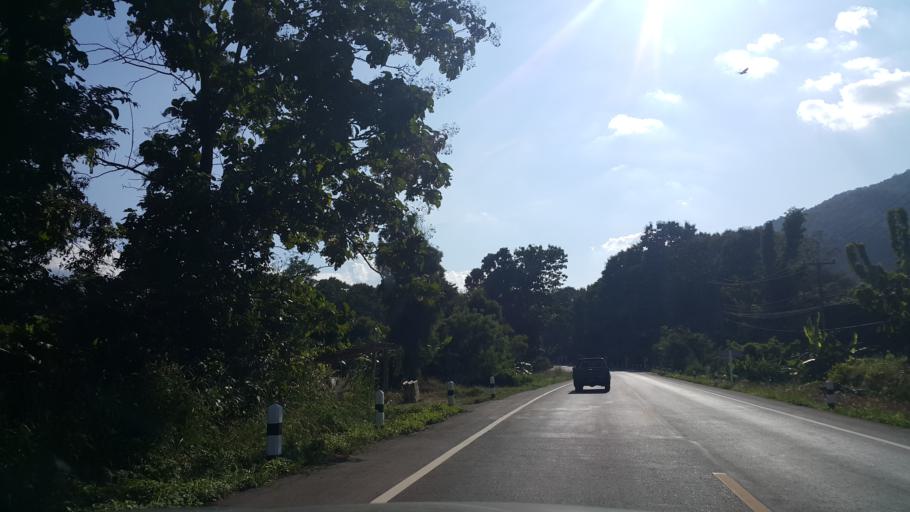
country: TH
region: Lamphun
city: Mae Tha
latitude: 18.5047
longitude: 99.2019
